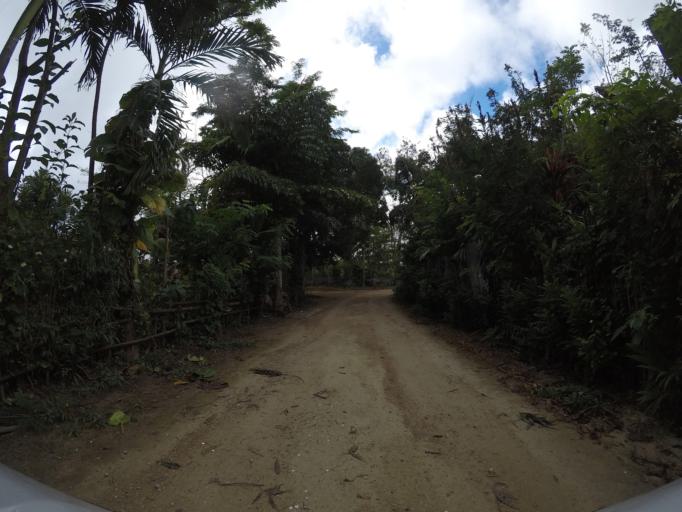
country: TL
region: Lautem
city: Lospalos
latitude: -8.4993
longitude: 127.0004
